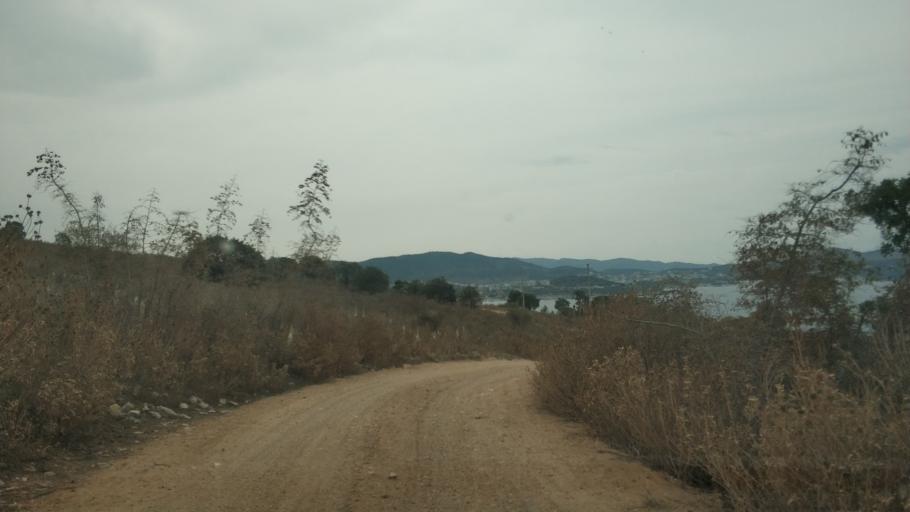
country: AL
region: Vlore
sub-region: Rrethi i Sarandes
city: Sarande
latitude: 39.7962
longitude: 20.0033
